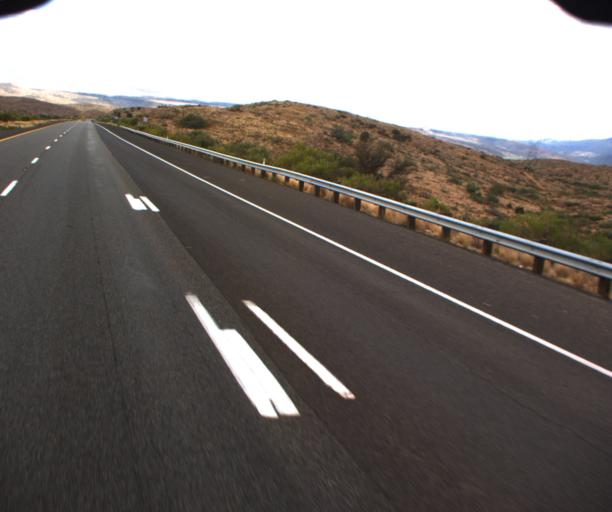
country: US
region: Arizona
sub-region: Yavapai County
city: Cordes Lakes
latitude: 34.2811
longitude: -112.1190
